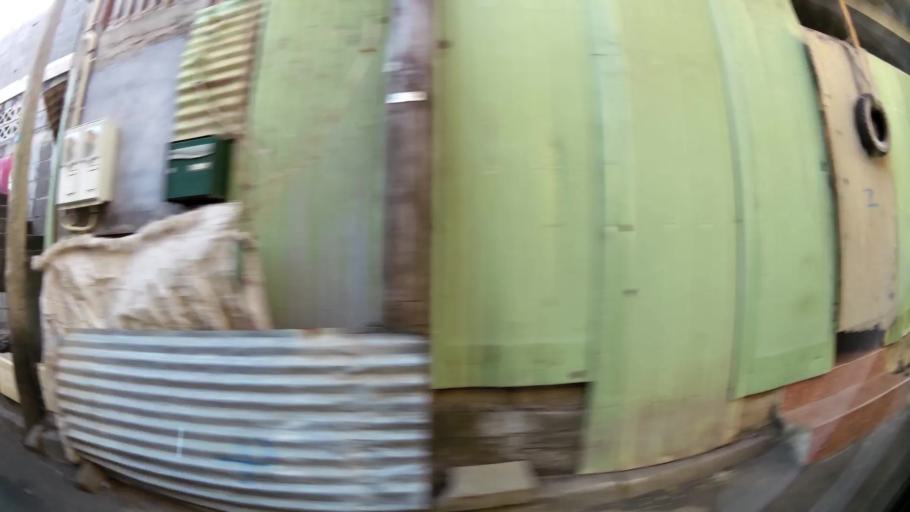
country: YT
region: Koungou
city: Koungou
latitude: -12.7364
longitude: 45.2060
